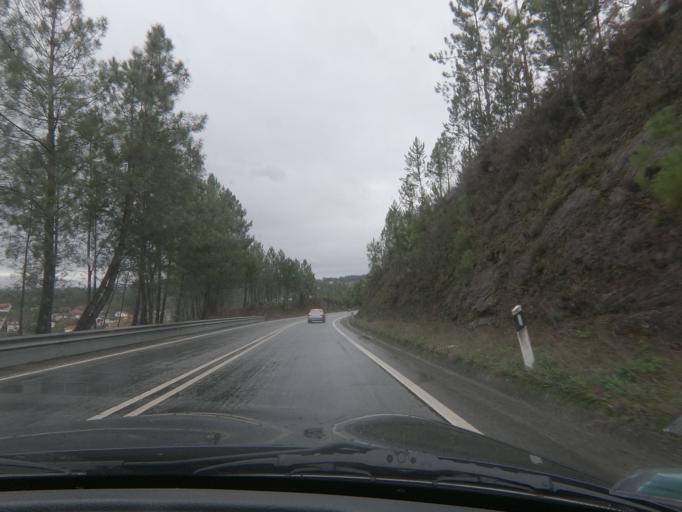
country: PT
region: Porto
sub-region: Amarante
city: Teloes
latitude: 41.3235
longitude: -8.0625
